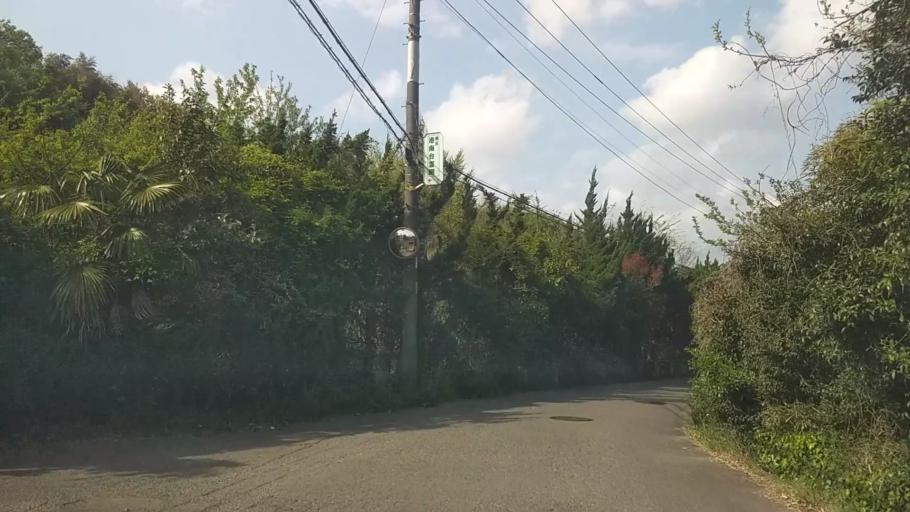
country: JP
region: Kanagawa
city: Kamakura
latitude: 35.3826
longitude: 139.5646
